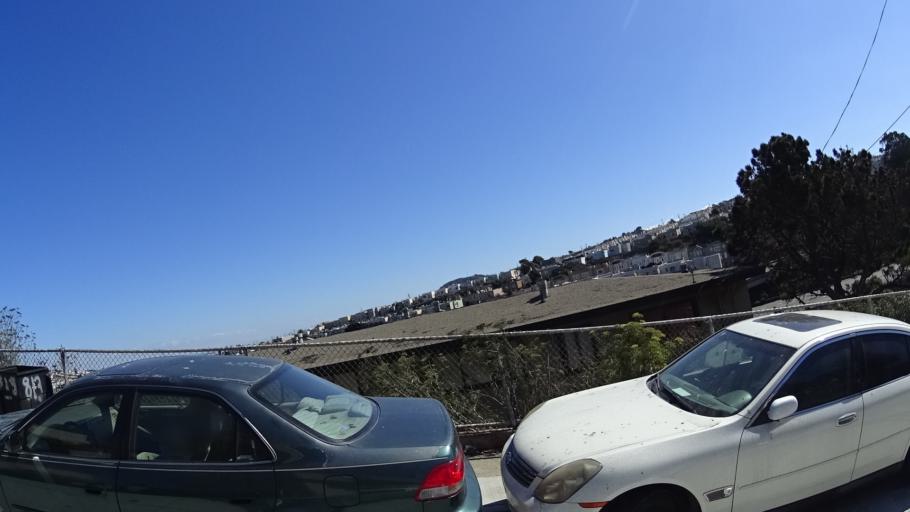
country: US
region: California
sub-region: San Francisco County
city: San Francisco
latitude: 37.7333
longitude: -122.4152
